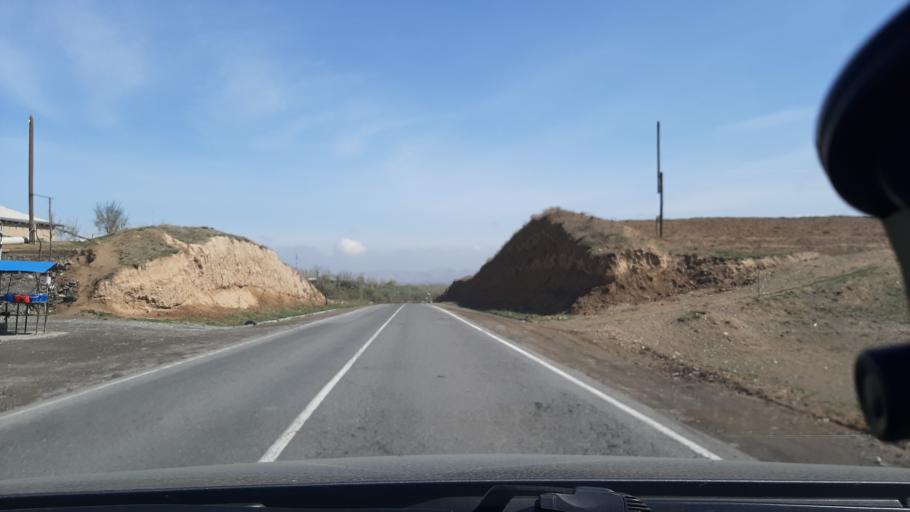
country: TJ
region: Viloyati Sughd
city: Shahriston
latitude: 39.7742
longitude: 68.8274
